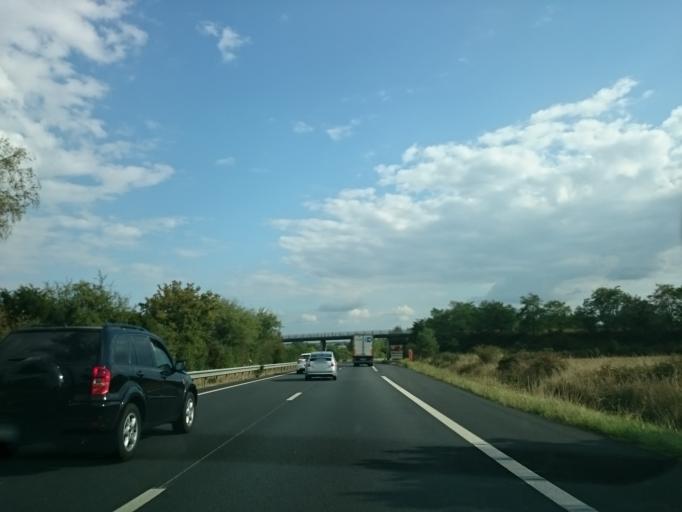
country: FR
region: Brittany
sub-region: Departement d'Ille-et-Vilaine
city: Grand-Fougeray
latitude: 47.7084
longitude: -1.7049
